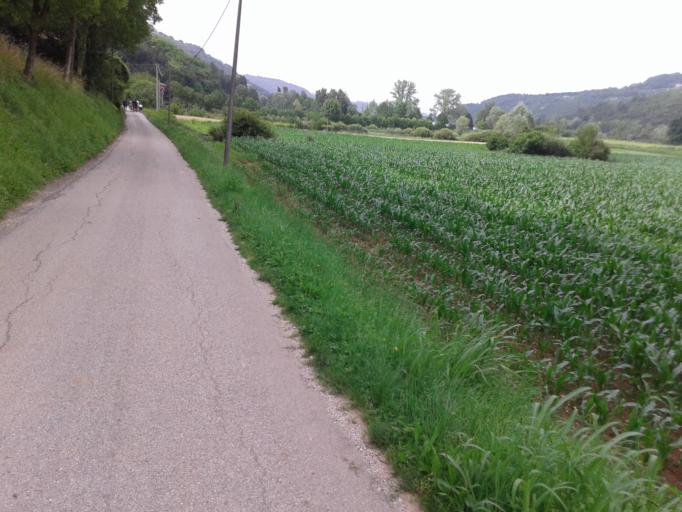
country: IT
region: Veneto
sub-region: Provincia di Vicenza
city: Arcugnano-Torri
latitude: 45.4593
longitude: 11.5400
